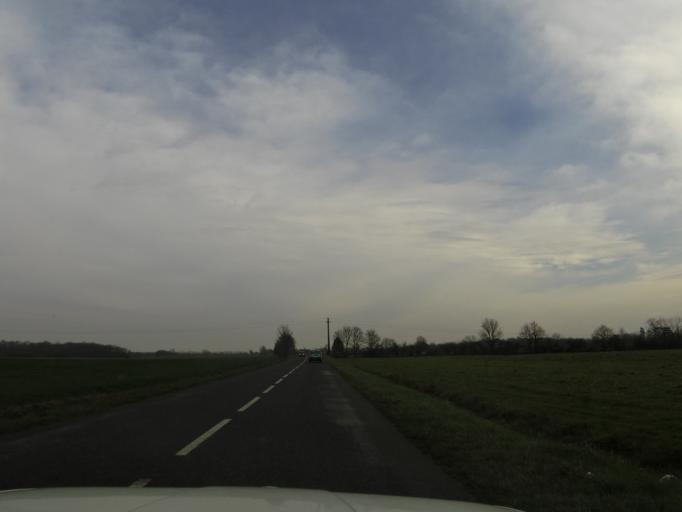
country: FR
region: Rhone-Alpes
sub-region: Departement de l'Ain
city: Villars-les-Dombes
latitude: 46.0771
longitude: 5.0372
